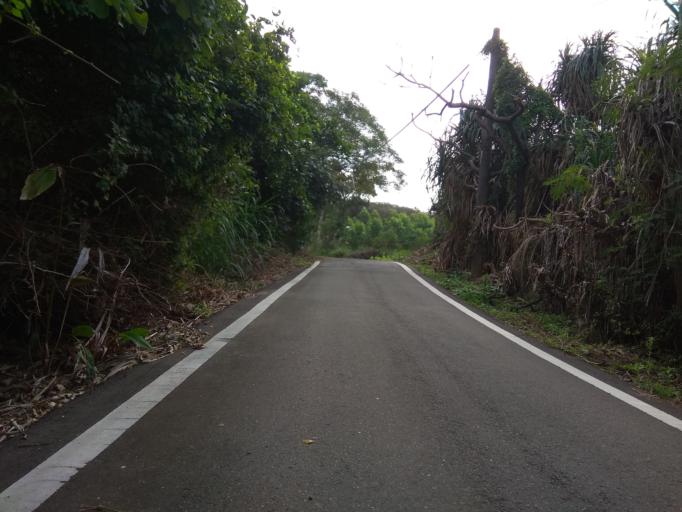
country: TW
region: Taiwan
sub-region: Hsinchu
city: Zhubei
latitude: 24.9526
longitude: 120.9986
